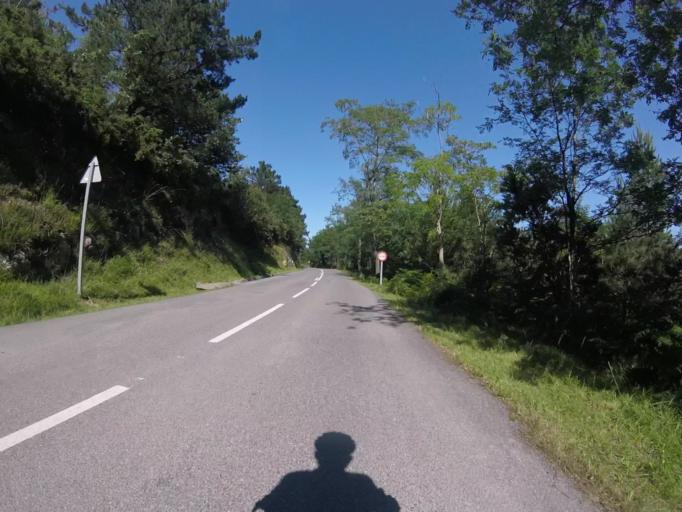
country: ES
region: Basque Country
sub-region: Provincia de Guipuzcoa
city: Irun
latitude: 43.3006
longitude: -1.8255
